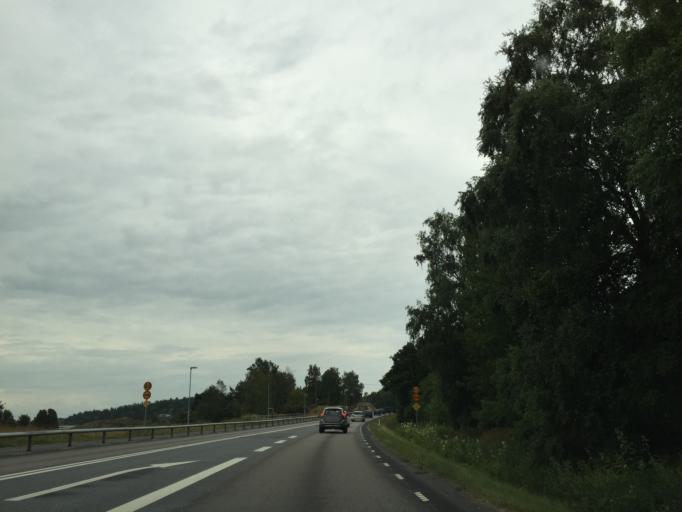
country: SE
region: Vaestra Goetaland
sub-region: Tjorns Kommun
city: Myggenas
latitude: 58.0566
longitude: 11.7596
